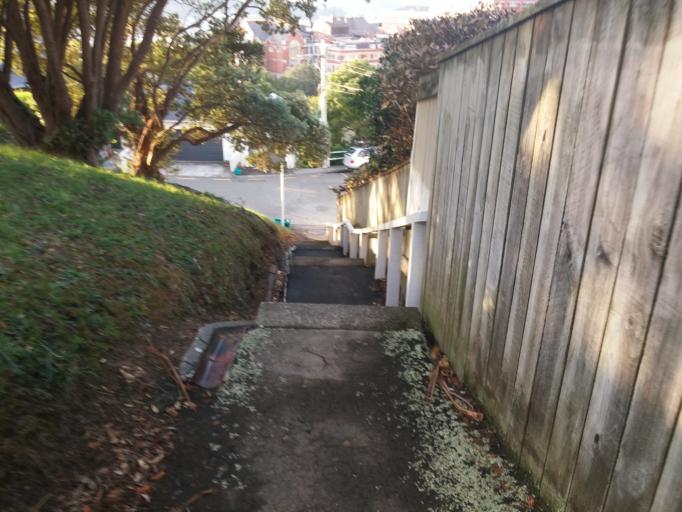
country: NZ
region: Wellington
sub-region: Wellington City
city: Kelburn
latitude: -41.2861
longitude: 174.7674
